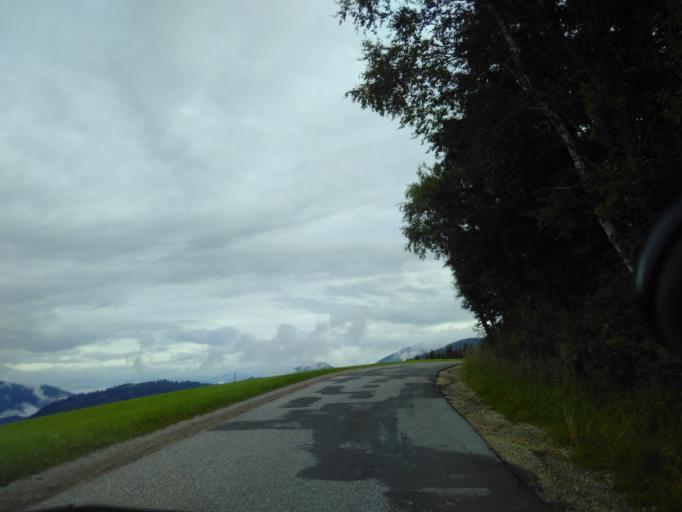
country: AT
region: Styria
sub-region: Politischer Bezirk Graz-Umgebung
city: Semriach
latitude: 47.2595
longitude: 15.4134
